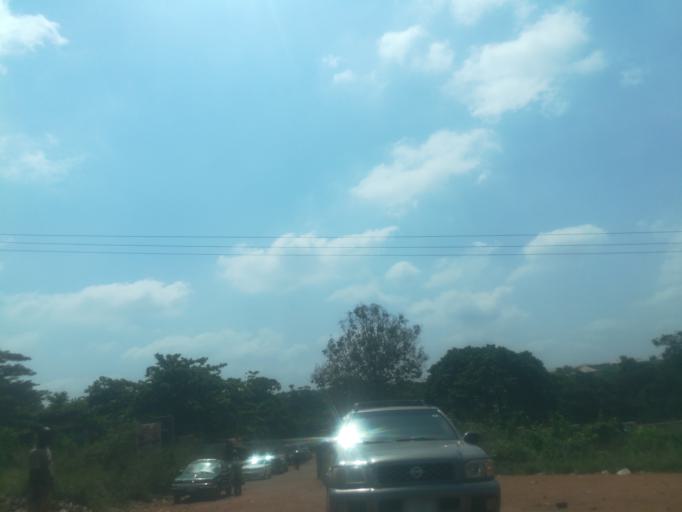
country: NG
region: Ogun
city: Abeokuta
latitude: 7.1402
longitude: 3.4004
